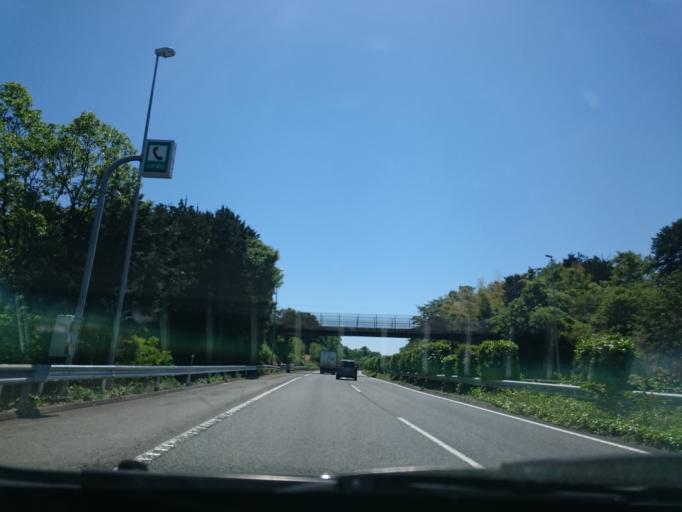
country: JP
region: Shizuoka
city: Mishima
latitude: 35.1710
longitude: 138.8965
